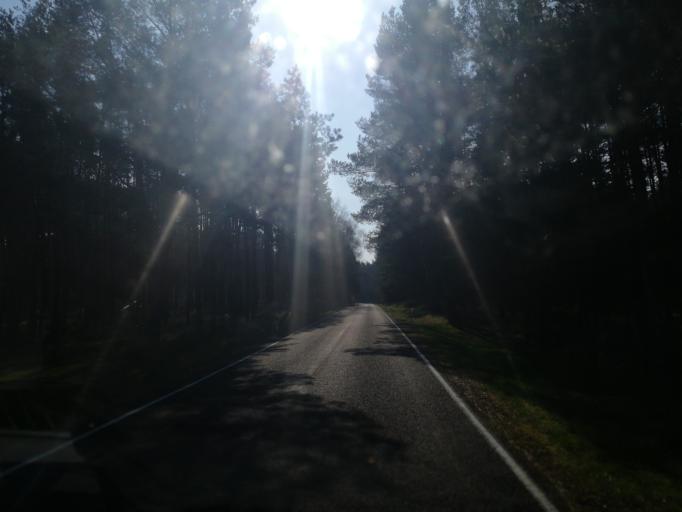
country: DE
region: Brandenburg
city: Sonnewalde
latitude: 51.7740
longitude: 13.6385
